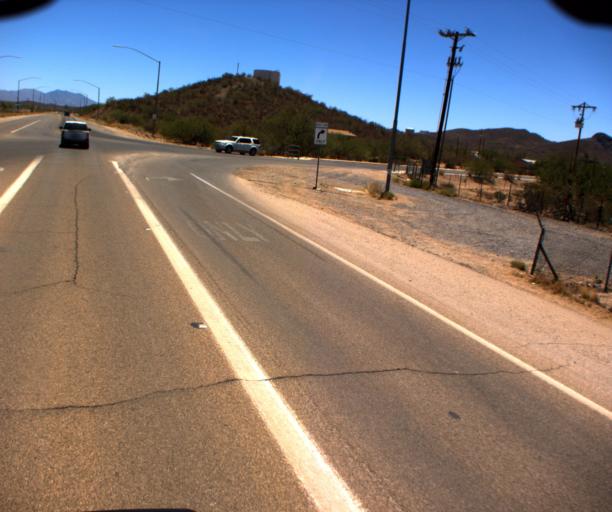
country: US
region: Arizona
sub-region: Pima County
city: Sells
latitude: 31.9214
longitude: -111.8905
